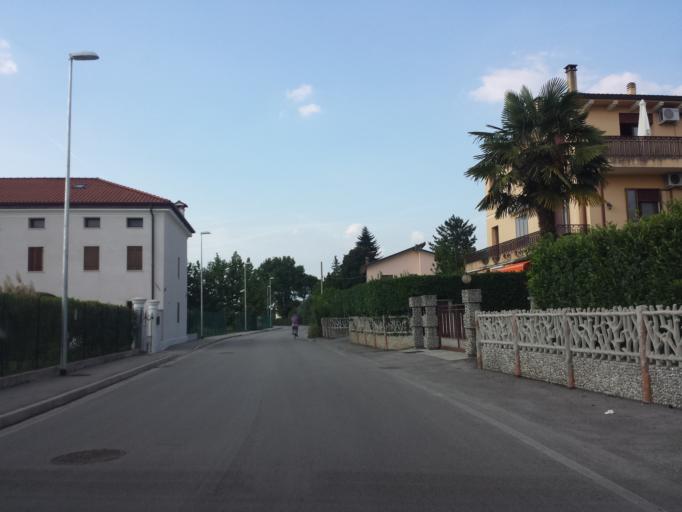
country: IT
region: Veneto
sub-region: Provincia di Vicenza
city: Villaggio Montegrappa
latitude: 45.5466
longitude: 11.6001
